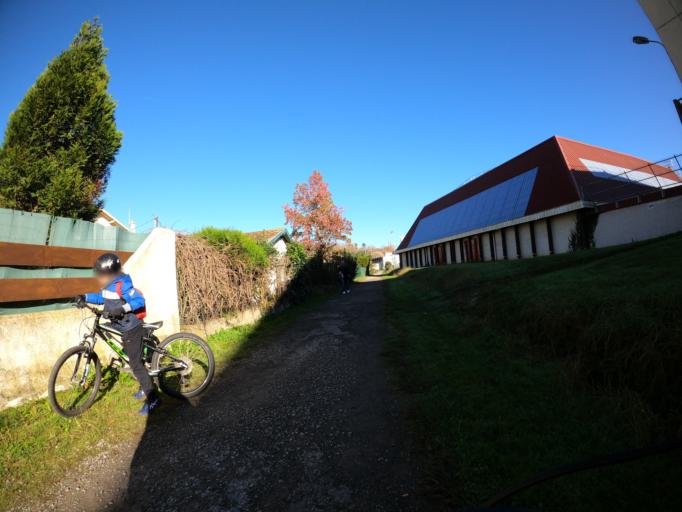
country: FR
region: Aquitaine
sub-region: Departement des Pyrenees-Atlantiques
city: Bayonne
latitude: 43.4954
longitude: -1.4599
